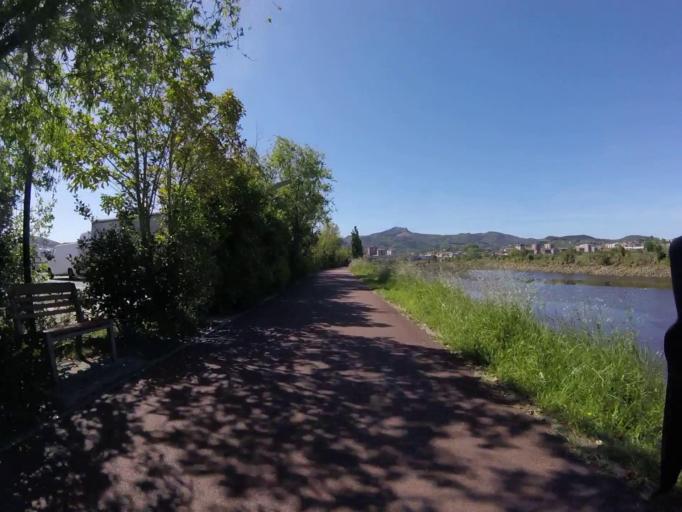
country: ES
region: Basque Country
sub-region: Provincia de Guipuzcoa
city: Irun
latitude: 43.3475
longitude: -1.7768
